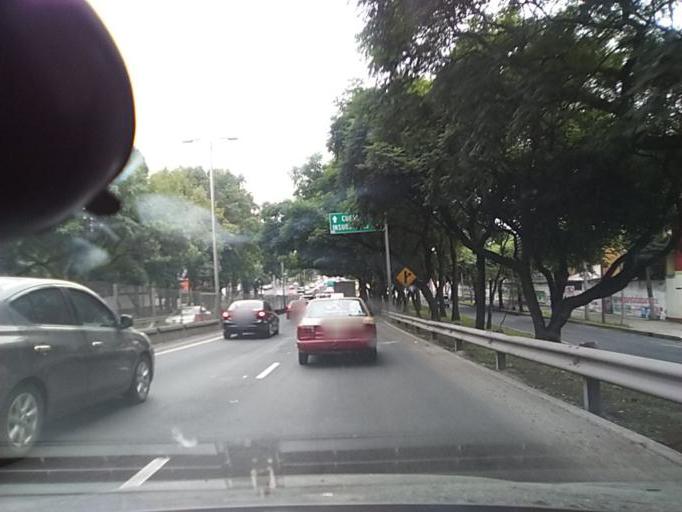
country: MX
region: Mexico City
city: Tlalpan
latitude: 19.2862
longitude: -99.1577
